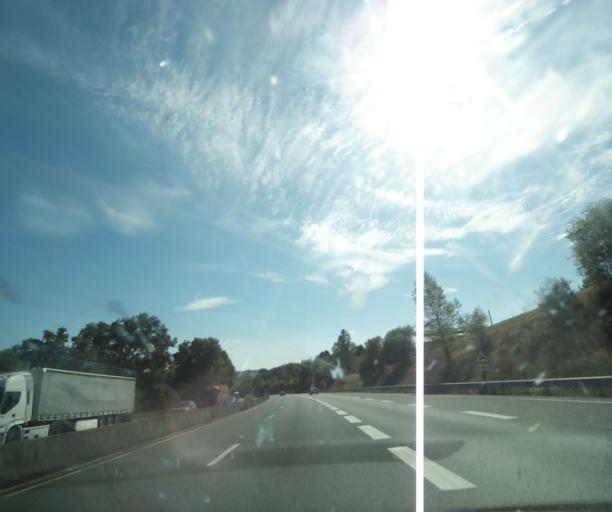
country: FR
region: Limousin
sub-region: Departement de la Correze
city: Donzenac
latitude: 45.2250
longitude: 1.5110
